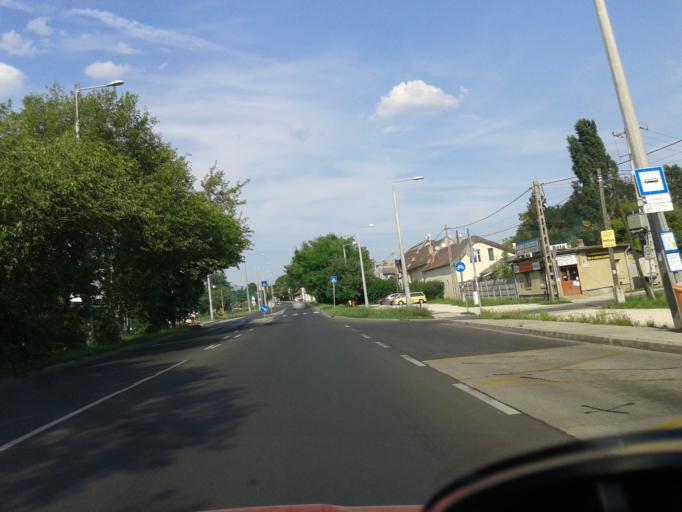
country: HU
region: Pest
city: Csomor
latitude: 47.5189
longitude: 19.2167
